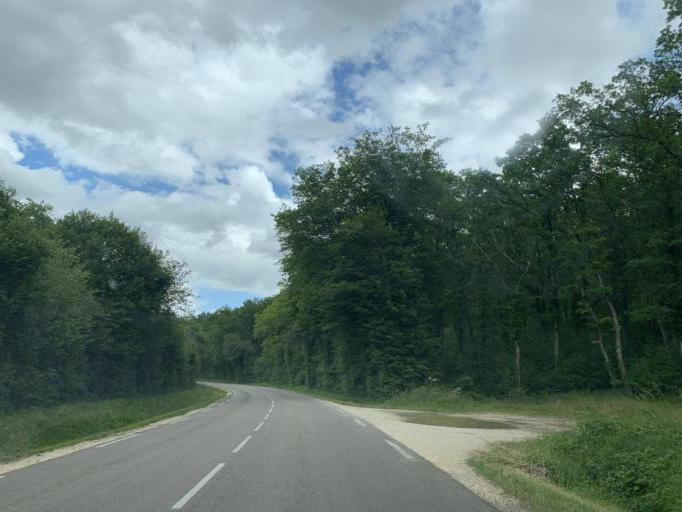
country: FR
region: Bourgogne
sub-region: Departement de l'Yonne
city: Chablis
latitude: 47.7391
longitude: 3.8151
